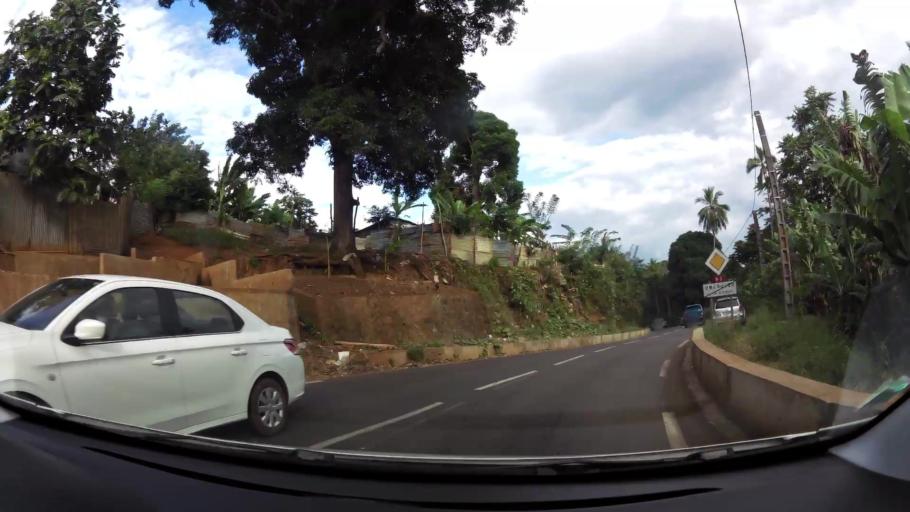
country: YT
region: Ouangani
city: Ouangani
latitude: -12.8369
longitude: 45.1584
